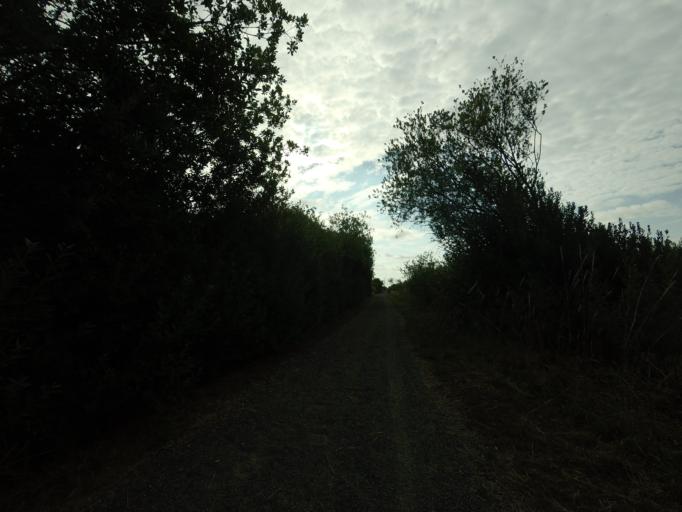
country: SE
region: Skane
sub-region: Helsingborg
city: Odakra
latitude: 56.1689
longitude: 12.7185
